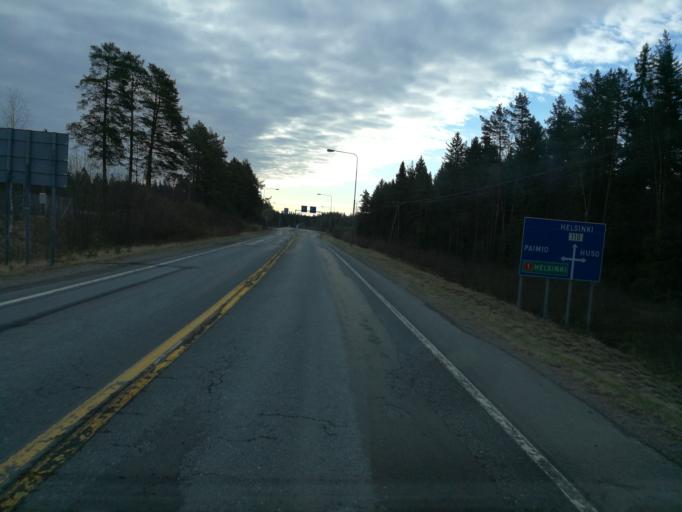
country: FI
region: Varsinais-Suomi
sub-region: Turku
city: Paimio
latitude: 60.4213
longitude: 22.7224
